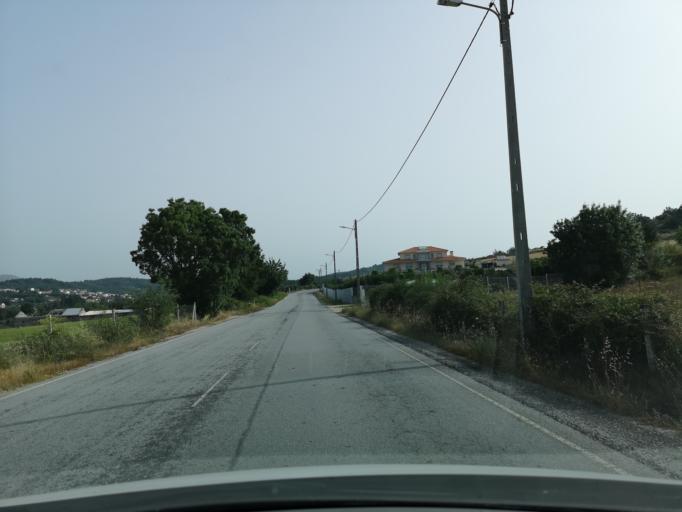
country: PT
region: Castelo Branco
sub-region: Belmonte
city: Belmonte
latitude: 40.3688
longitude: -7.3331
